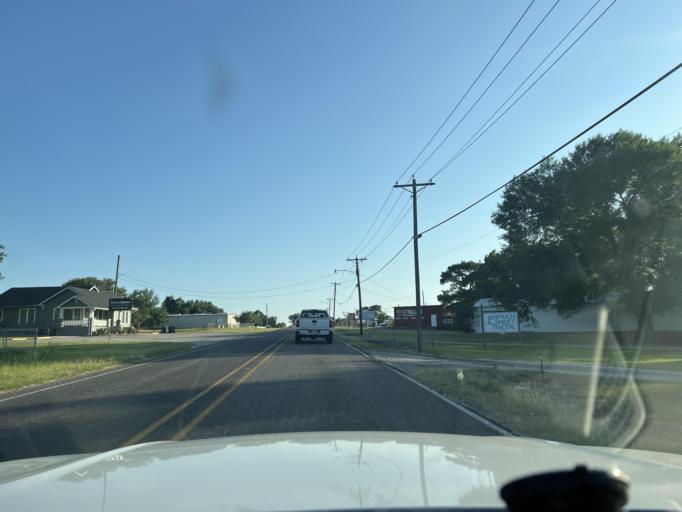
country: US
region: Texas
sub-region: Washington County
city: Brenham
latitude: 30.1758
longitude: -96.3875
